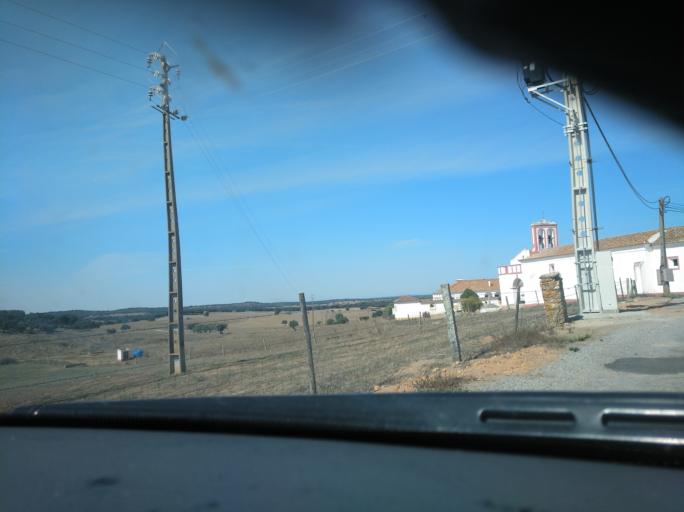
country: PT
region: Evora
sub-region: Arraiolos
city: Arraiolos
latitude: 38.7081
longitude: -8.0998
